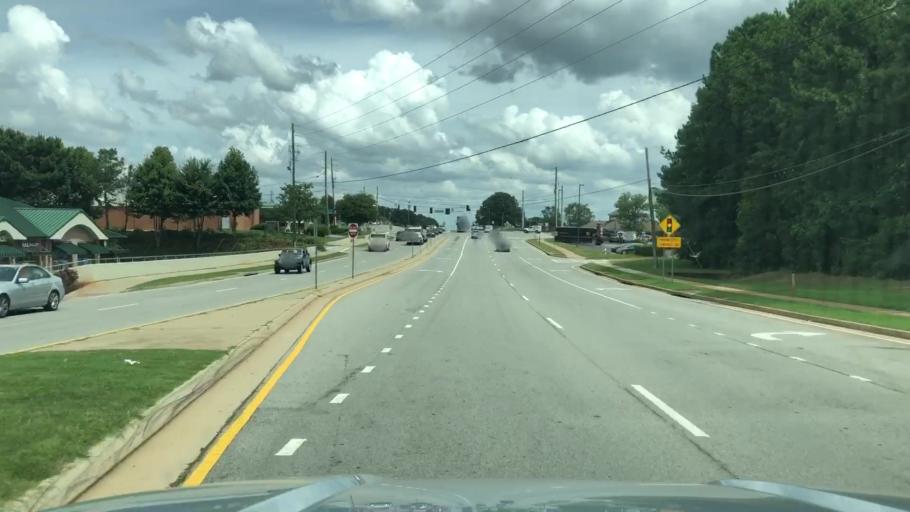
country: US
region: Georgia
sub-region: Gwinnett County
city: Suwanee
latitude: 34.0257
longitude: -84.0469
